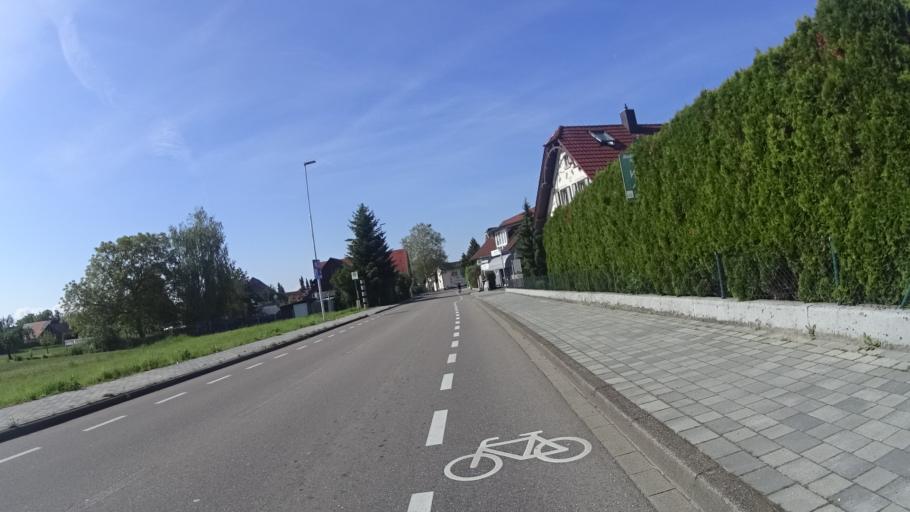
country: DE
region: Baden-Wuerttemberg
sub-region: Freiburg Region
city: Kehl
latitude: 48.5246
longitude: 7.8252
